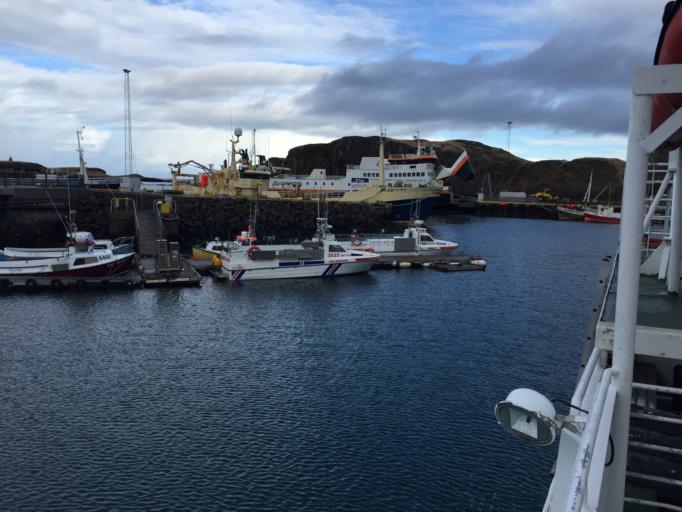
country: IS
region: West
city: Stykkisholmur
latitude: 65.0784
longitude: -22.7257
